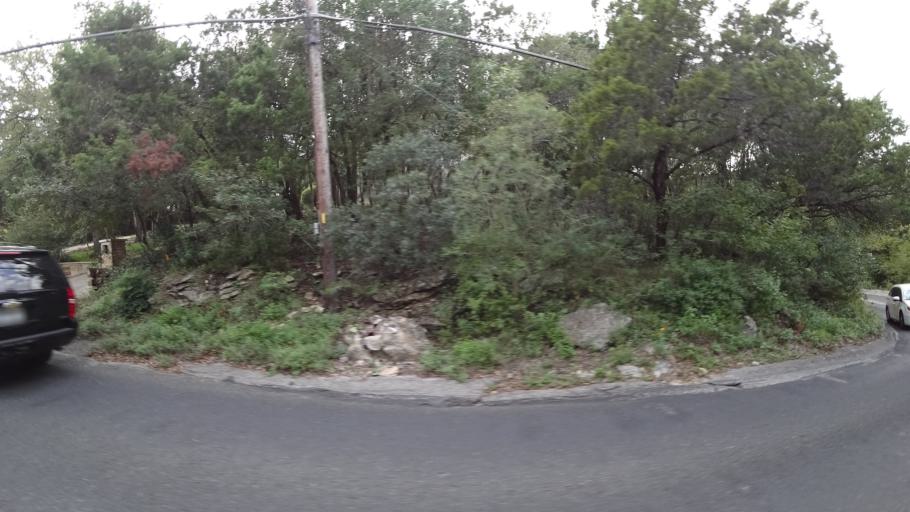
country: US
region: Texas
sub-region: Travis County
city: Rollingwood
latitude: 30.2840
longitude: -97.7871
